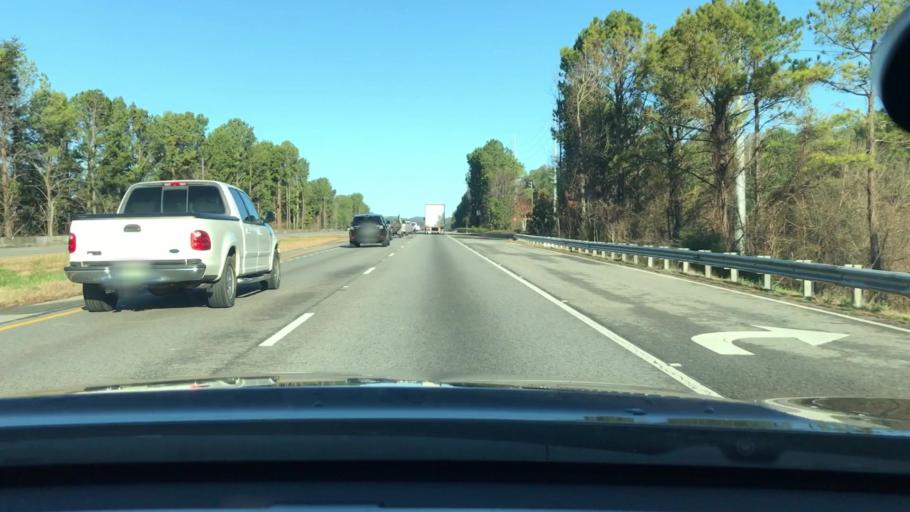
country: US
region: Alabama
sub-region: Shelby County
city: Chelsea
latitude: 33.3622
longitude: -86.6572
